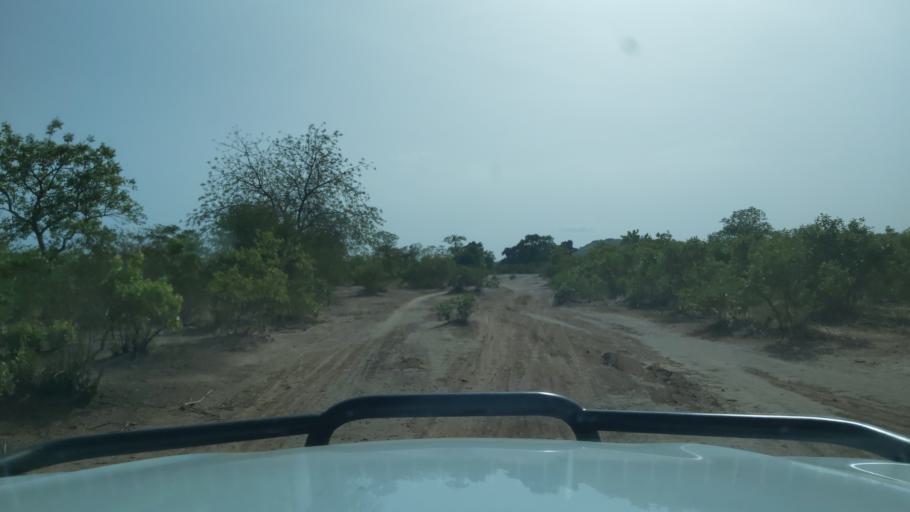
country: ML
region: Koulikoro
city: Koulikoro
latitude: 13.1762
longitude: -7.7517
